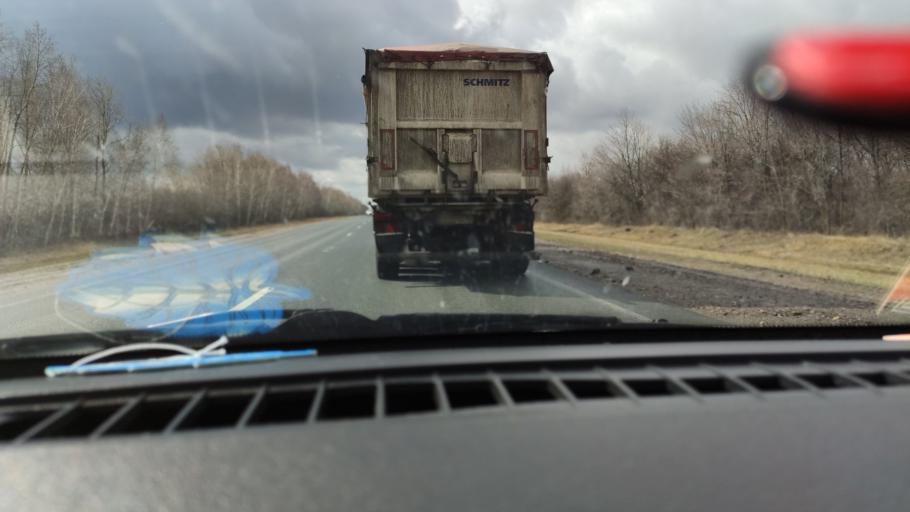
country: RU
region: Samara
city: Yelkhovka
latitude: 53.9522
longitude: 50.2683
